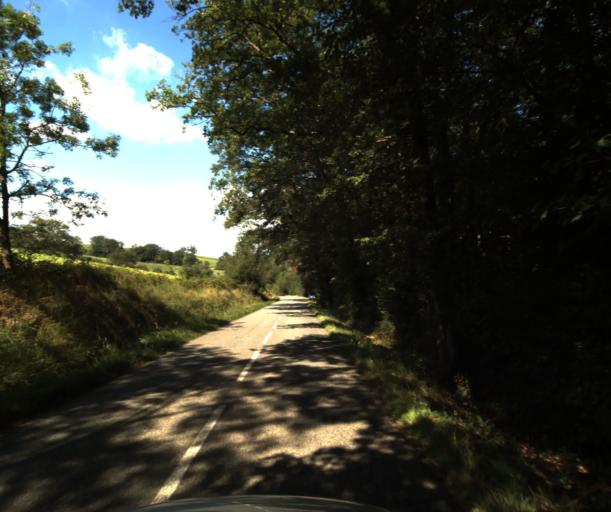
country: FR
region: Midi-Pyrenees
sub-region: Departement de la Haute-Garonne
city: Eaunes
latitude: 43.4133
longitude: 1.3361
